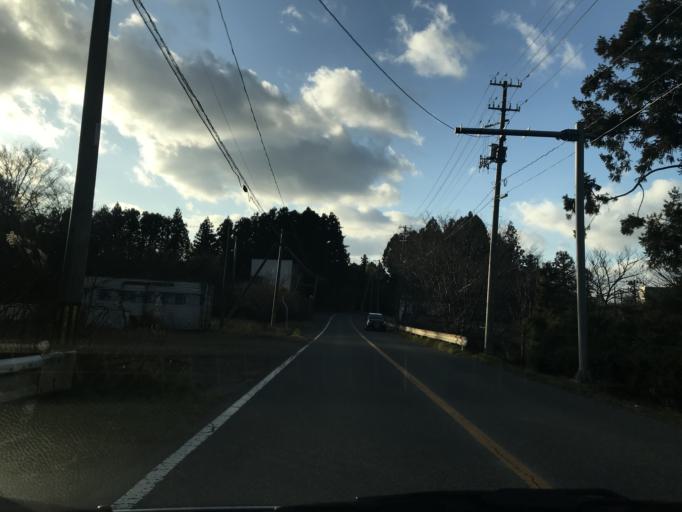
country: JP
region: Miyagi
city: Wakuya
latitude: 38.6699
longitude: 141.1001
